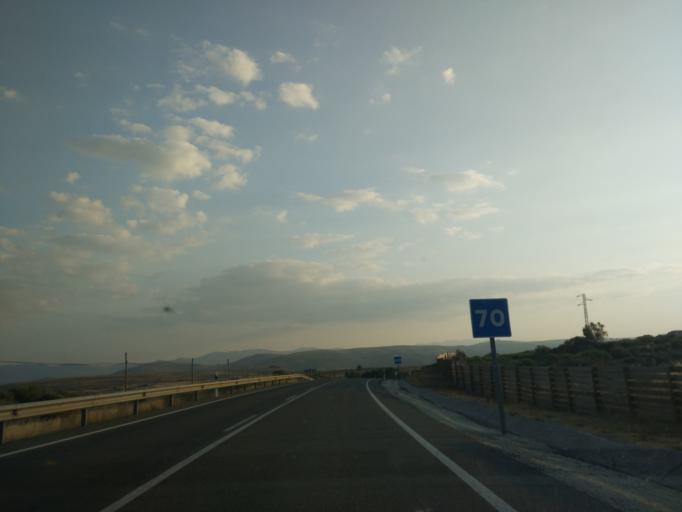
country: ES
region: Castille and Leon
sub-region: Provincia de Avila
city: Cepeda la Mora
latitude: 40.4610
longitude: -5.0243
